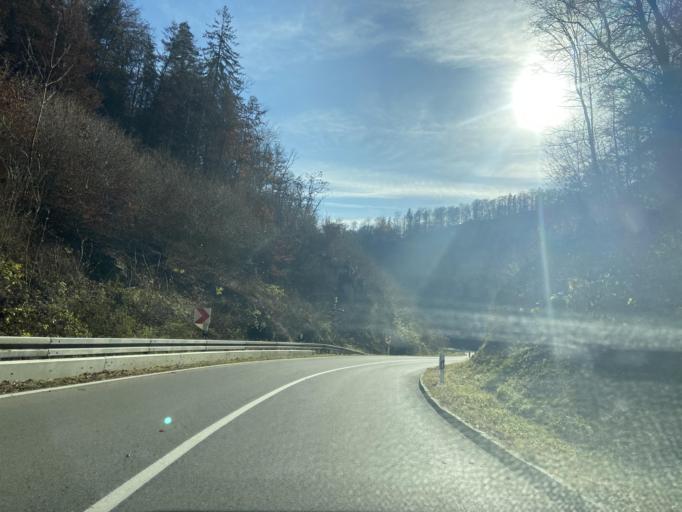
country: DE
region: Baden-Wuerttemberg
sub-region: Tuebingen Region
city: Stetten am Kalten Markt
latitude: 48.0940
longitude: 9.0915
